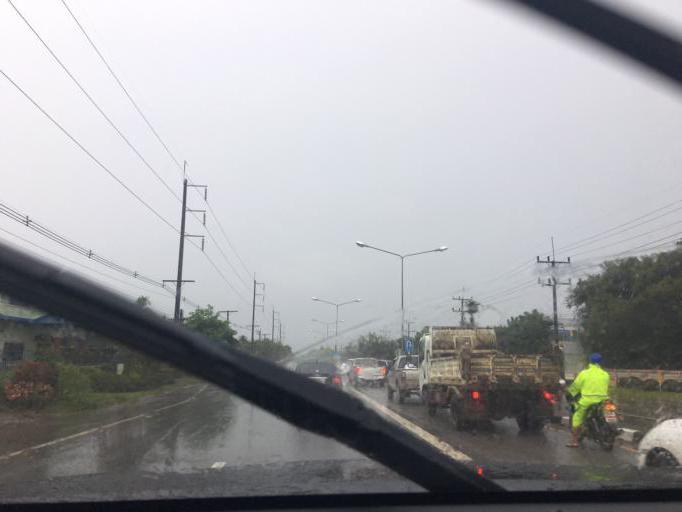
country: TH
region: Chiang Rai
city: Mae Fa Luang
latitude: 20.2592
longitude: 99.8563
